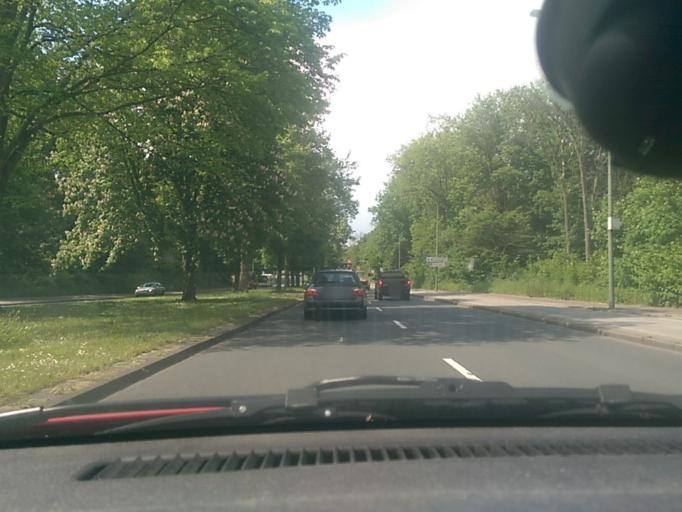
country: DE
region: North Rhine-Westphalia
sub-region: Regierungsbezirk Munster
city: Gladbeck
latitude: 51.5275
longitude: 7.0377
